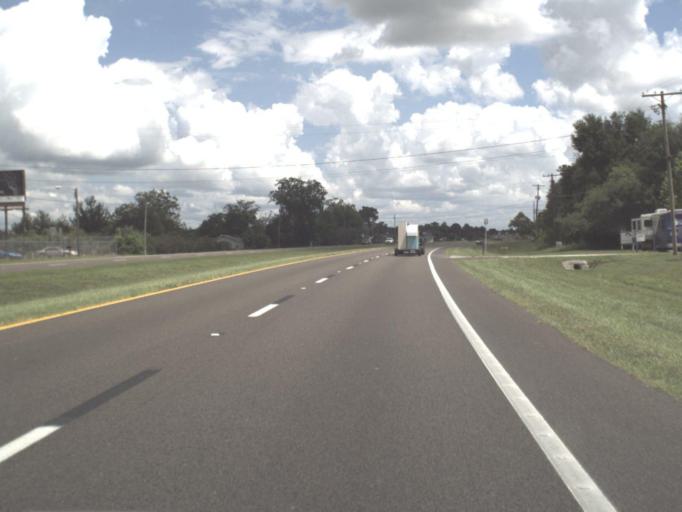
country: US
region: Florida
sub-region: Polk County
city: Haines City
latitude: 28.1080
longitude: -81.6696
